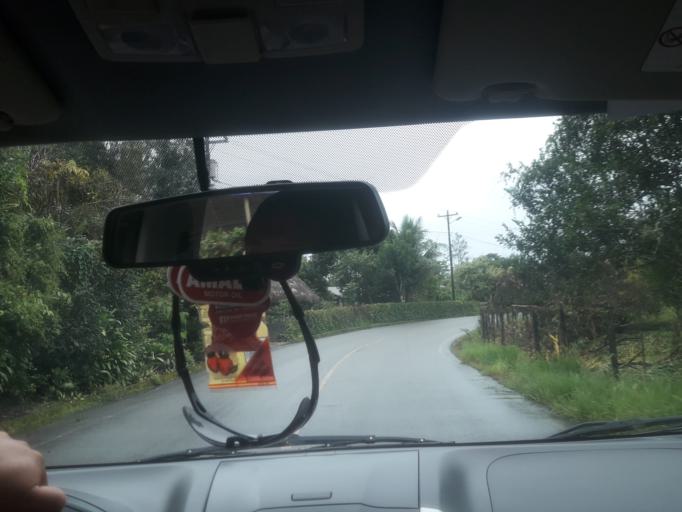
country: EC
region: Napo
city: Tena
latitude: -1.0342
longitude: -77.7473
